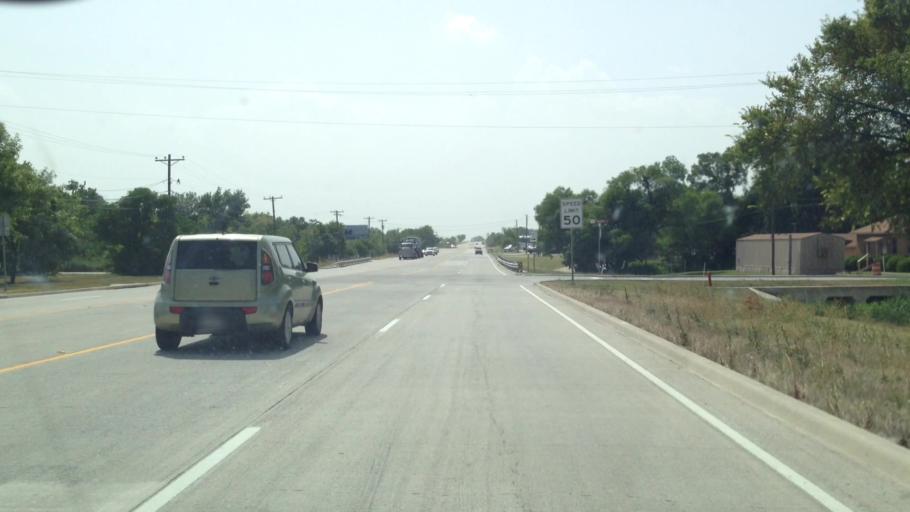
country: US
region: Texas
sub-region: Collin County
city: Farmersville
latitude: 33.1568
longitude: -96.3666
